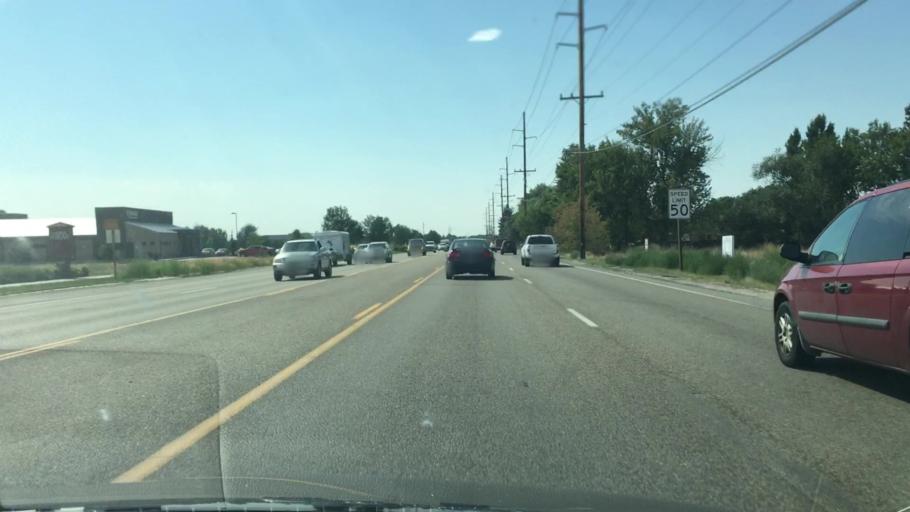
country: US
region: Idaho
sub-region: Ada County
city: Eagle
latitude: 43.6804
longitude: -116.3075
